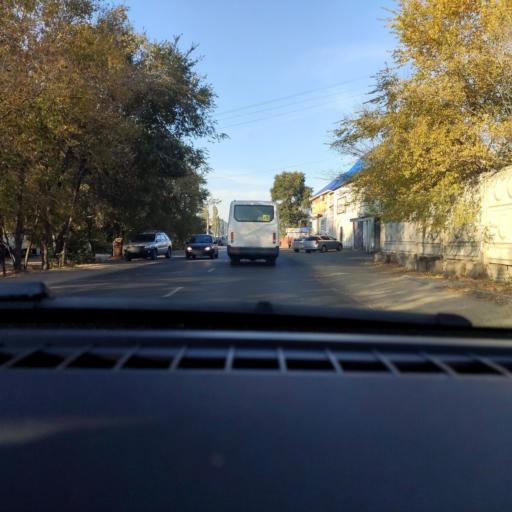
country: RU
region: Voronezj
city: Maslovka
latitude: 51.5965
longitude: 39.2490
